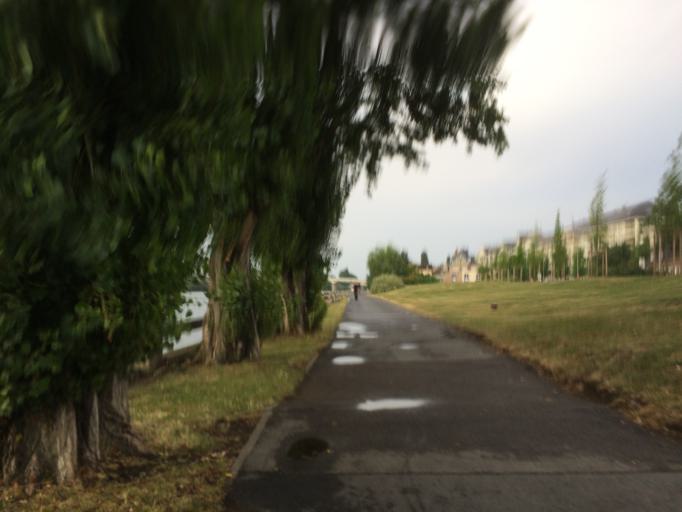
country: FR
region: Picardie
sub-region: Departement de l'Oise
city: Venette
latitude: 49.4145
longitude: 2.8134
